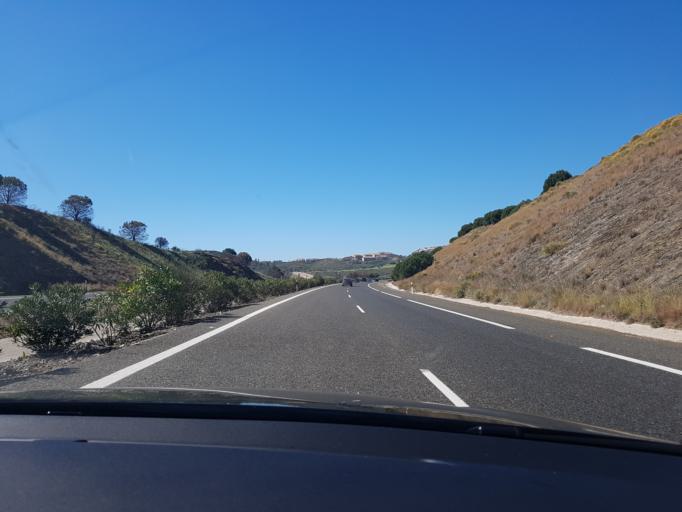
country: ES
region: Andalusia
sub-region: Provincia de Malaga
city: Fuengirola
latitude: 36.5190
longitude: -4.6890
